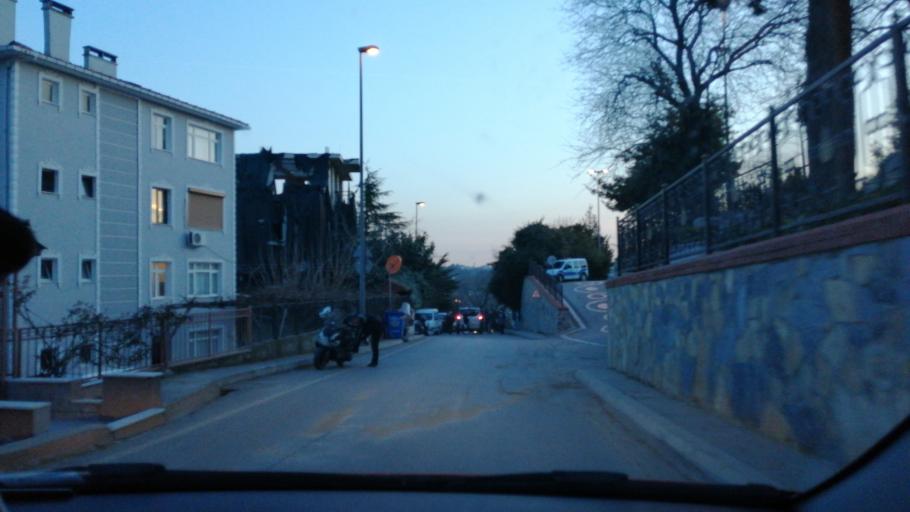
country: TR
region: Istanbul
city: UEskuedar
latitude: 41.0537
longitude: 29.0575
